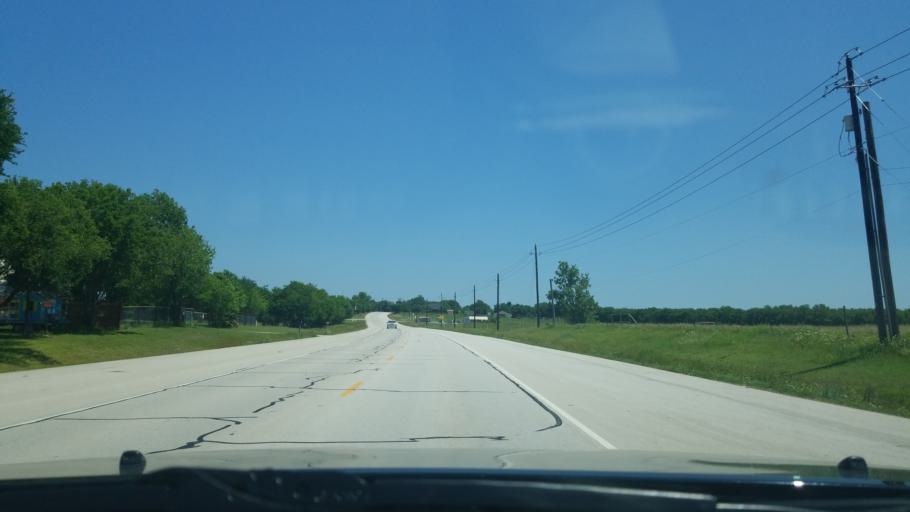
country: US
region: Texas
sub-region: Denton County
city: Krum
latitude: 33.2518
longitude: -97.2419
